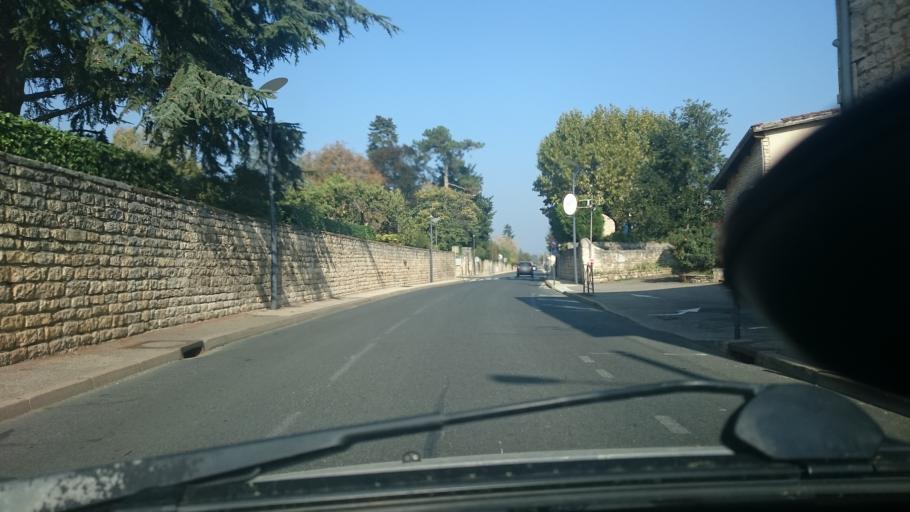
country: FR
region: Rhone-Alpes
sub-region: Departement du Rhone
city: Lucenay
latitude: 45.9132
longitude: 4.7026
